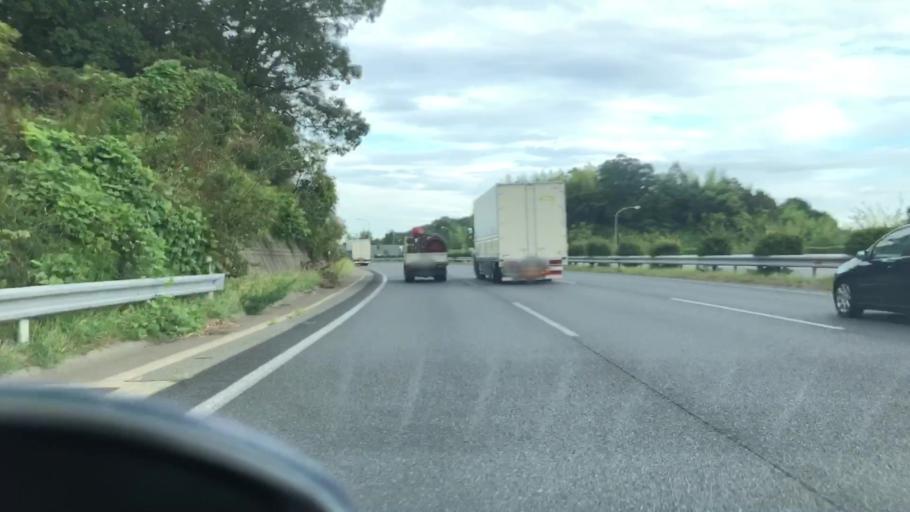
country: JP
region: Hyogo
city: Sandacho
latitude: 34.8857
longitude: 135.1643
